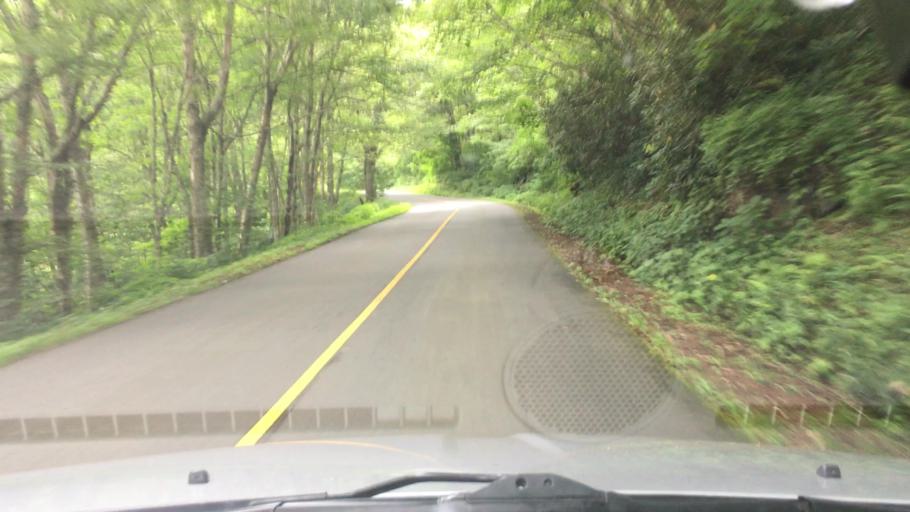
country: US
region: North Carolina
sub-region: Buncombe County
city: Swannanoa
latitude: 35.7014
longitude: -82.3941
